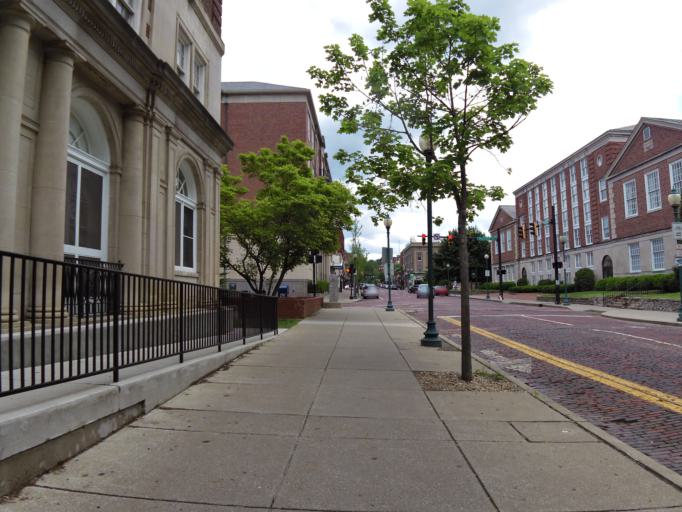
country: US
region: Ohio
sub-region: Athens County
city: Athens
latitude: 39.3263
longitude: -82.1015
